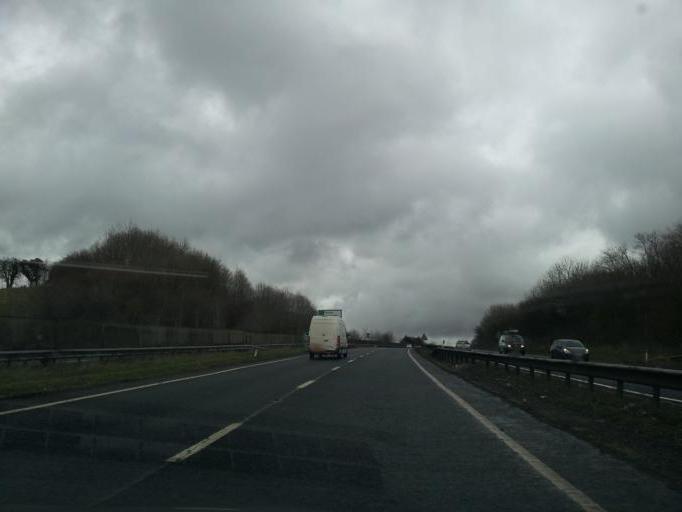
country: GB
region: England
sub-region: Somerset
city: Wincanton
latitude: 51.0678
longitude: -2.3625
